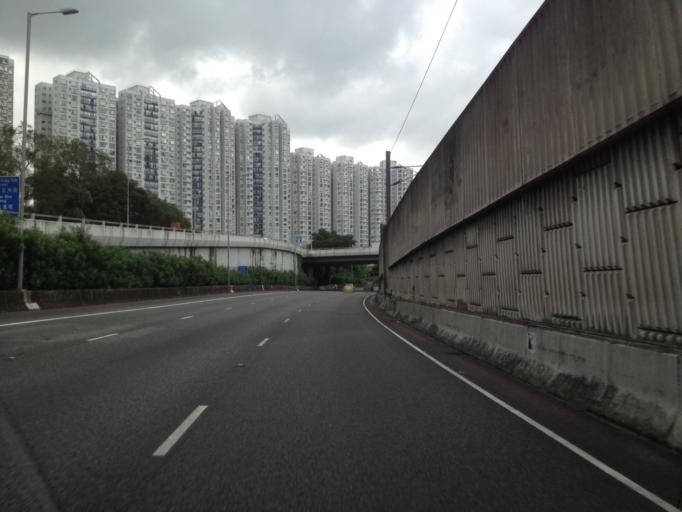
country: HK
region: Sha Tin
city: Sha Tin
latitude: 22.3923
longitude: 114.2093
